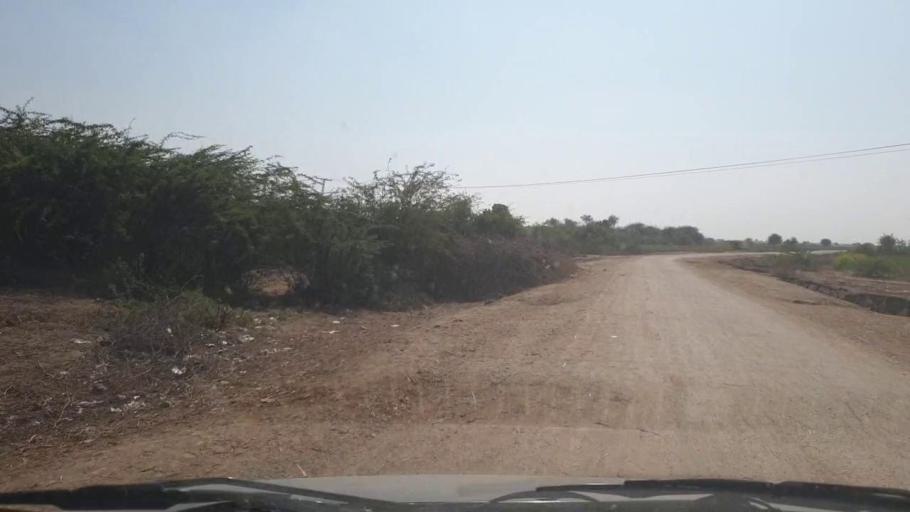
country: PK
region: Sindh
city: Samaro
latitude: 25.2261
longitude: 69.3227
